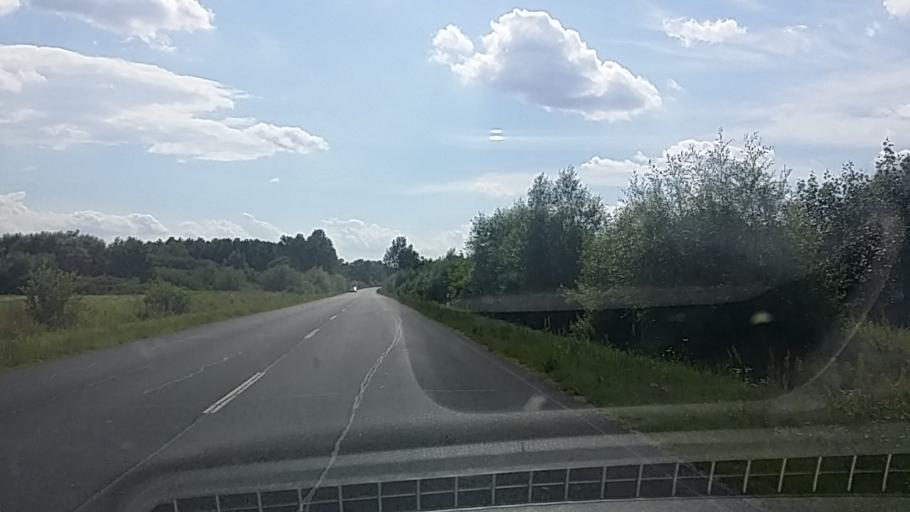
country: HU
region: Zala
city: Nagykanizsa
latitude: 46.4648
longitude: 16.9531
